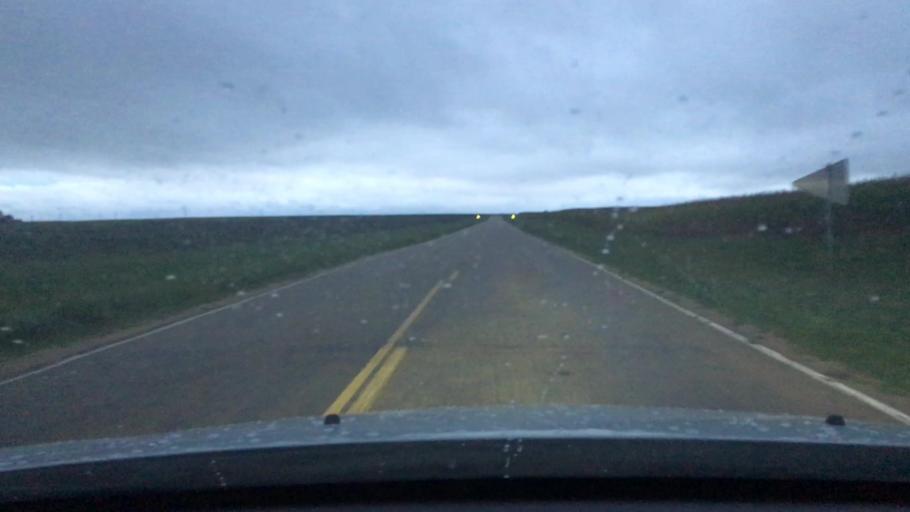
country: US
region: Illinois
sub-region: DeKalb County
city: Malta
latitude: 41.8986
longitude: -88.9608
